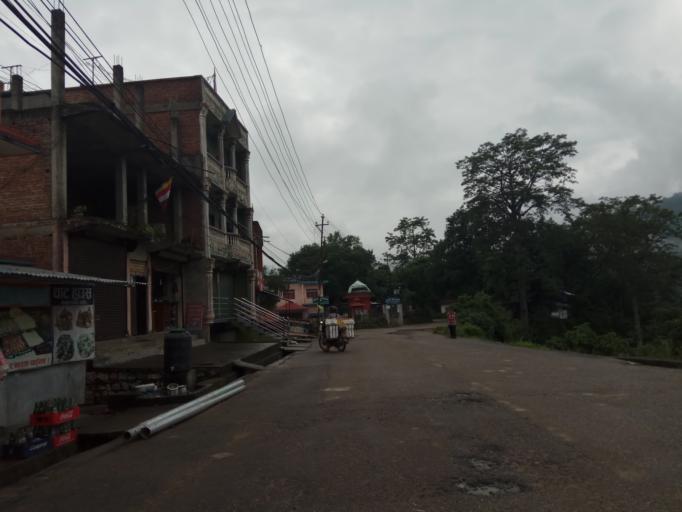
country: NP
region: Central Region
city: Kirtipur
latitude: 27.9093
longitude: 84.8997
